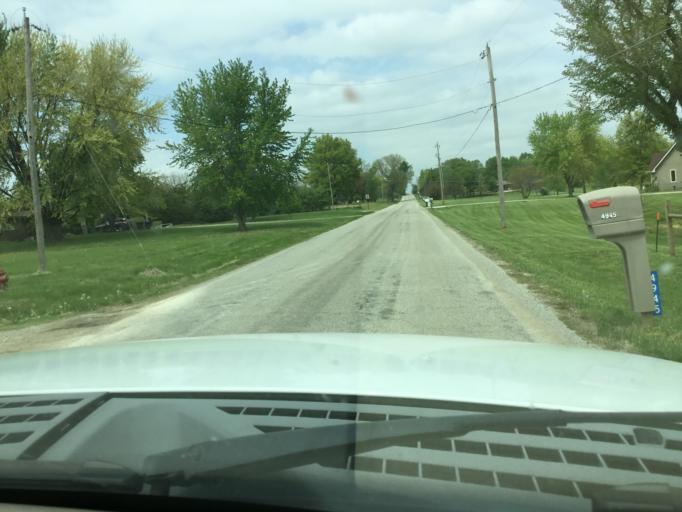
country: US
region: Kansas
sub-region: Shawnee County
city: Topeka
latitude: 38.9770
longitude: -95.5863
